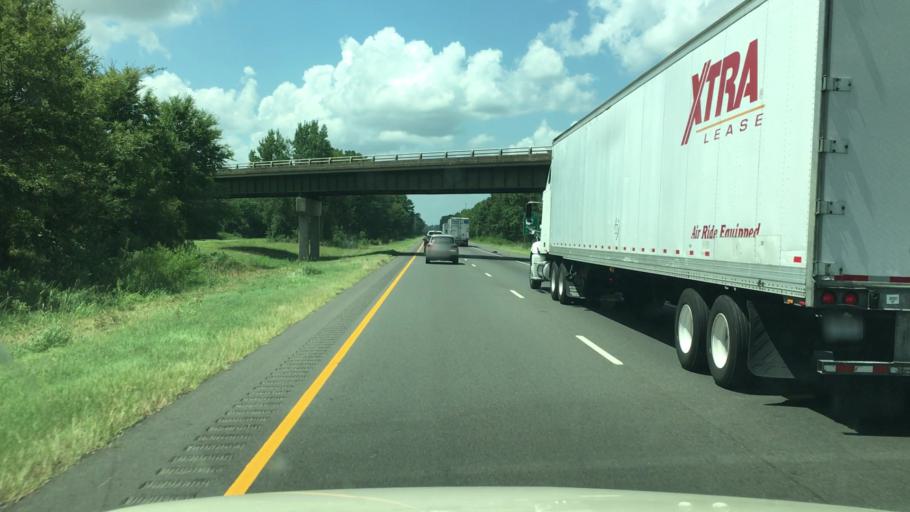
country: US
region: Arkansas
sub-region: Hempstead County
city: Hope
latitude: 33.7039
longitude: -93.5808
